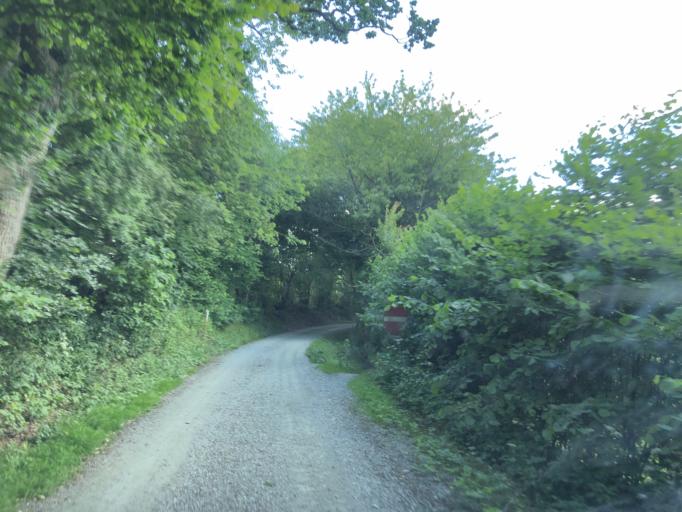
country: DK
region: South Denmark
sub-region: Vejle Kommune
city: Brejning
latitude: 55.6748
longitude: 9.6577
